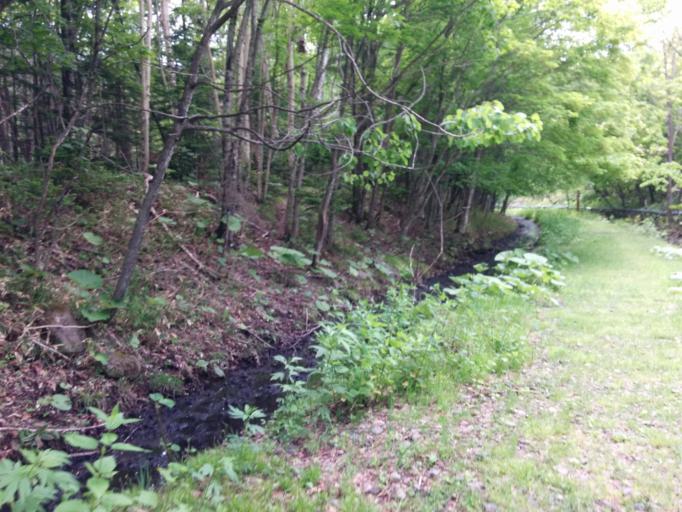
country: JP
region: Hokkaido
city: Otofuke
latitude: 43.3670
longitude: 143.1936
